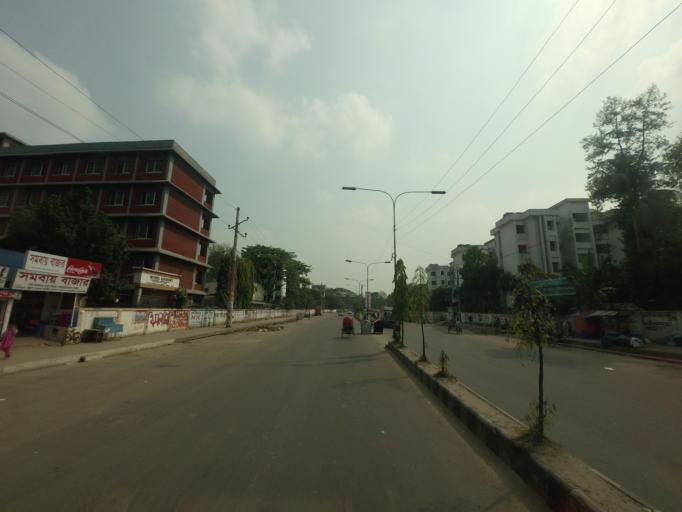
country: BD
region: Dhaka
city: Azimpur
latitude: 23.7868
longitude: 90.3540
